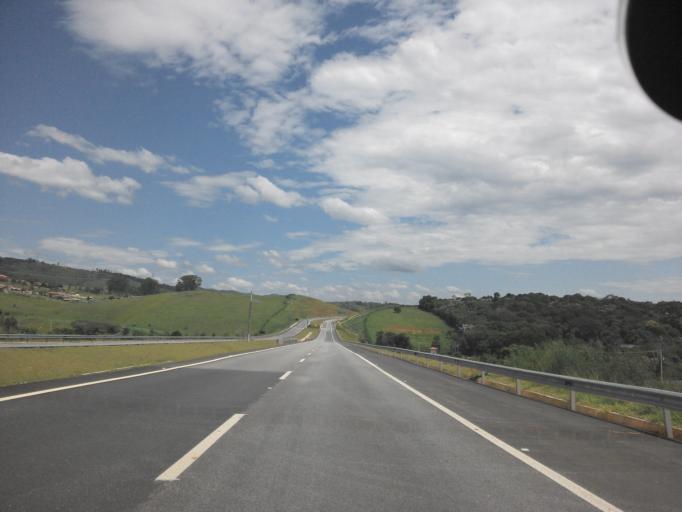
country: BR
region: Sao Paulo
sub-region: Taubate
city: Taubate
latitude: -23.0968
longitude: -45.5861
